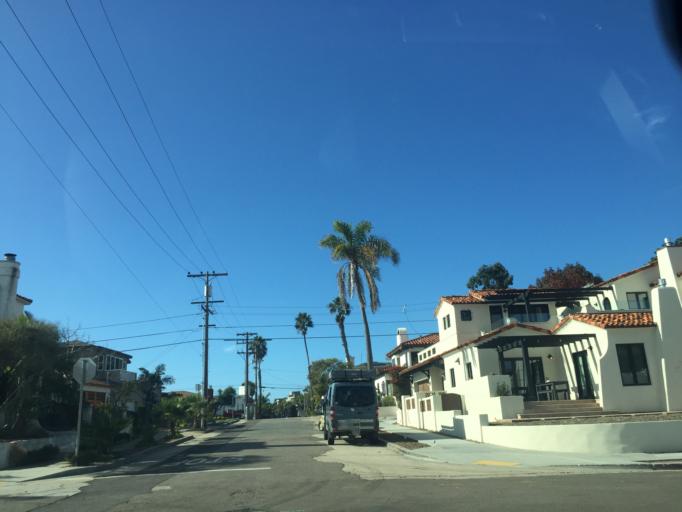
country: US
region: California
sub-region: San Diego County
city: La Jolla
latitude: 32.7826
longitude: -117.2351
